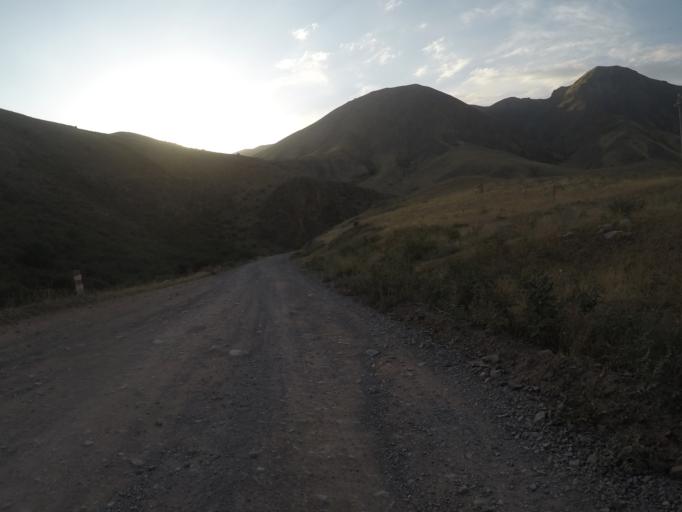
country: KG
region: Chuy
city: Bishkek
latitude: 42.6691
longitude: 74.6468
